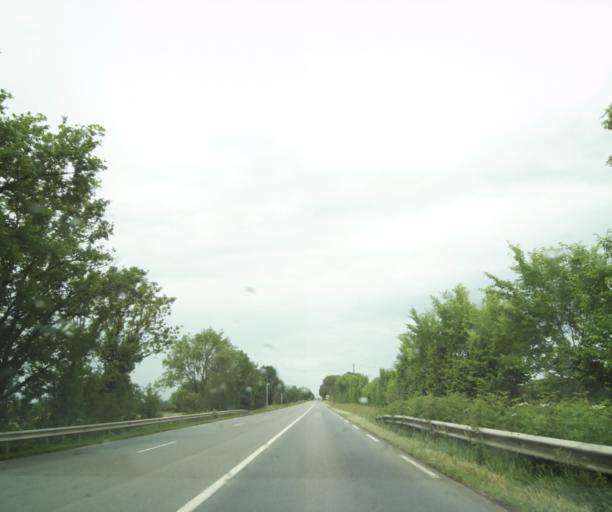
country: FR
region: Poitou-Charentes
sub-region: Departement des Deux-Sevres
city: Le Tallud
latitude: 46.6070
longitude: -0.2861
